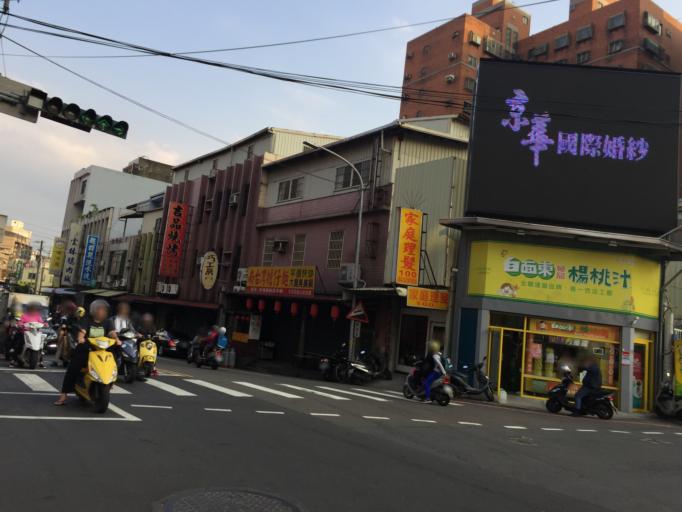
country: TW
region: Taiwan
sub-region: Hsinchu
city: Hsinchu
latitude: 24.7993
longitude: 120.9535
